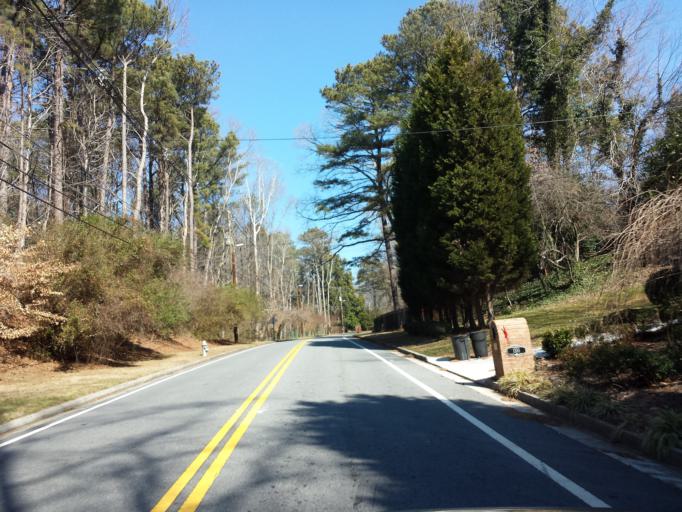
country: US
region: Georgia
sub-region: Fulton County
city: Sandy Springs
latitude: 33.9170
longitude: -84.4335
